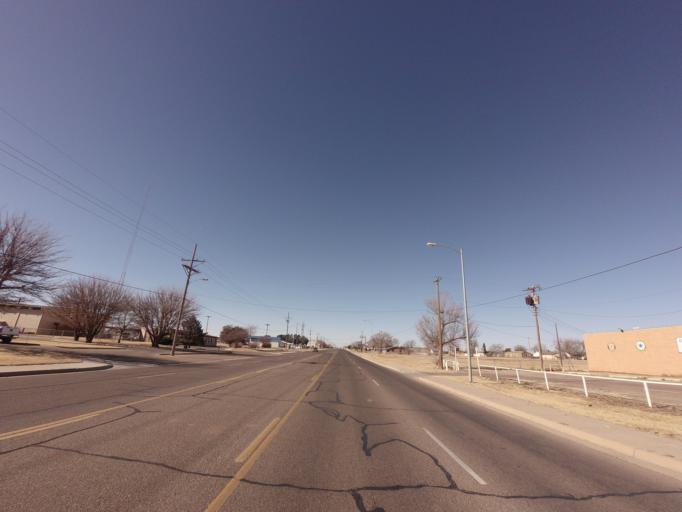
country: US
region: New Mexico
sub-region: Curry County
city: Clovis
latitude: 34.4047
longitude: -103.2354
